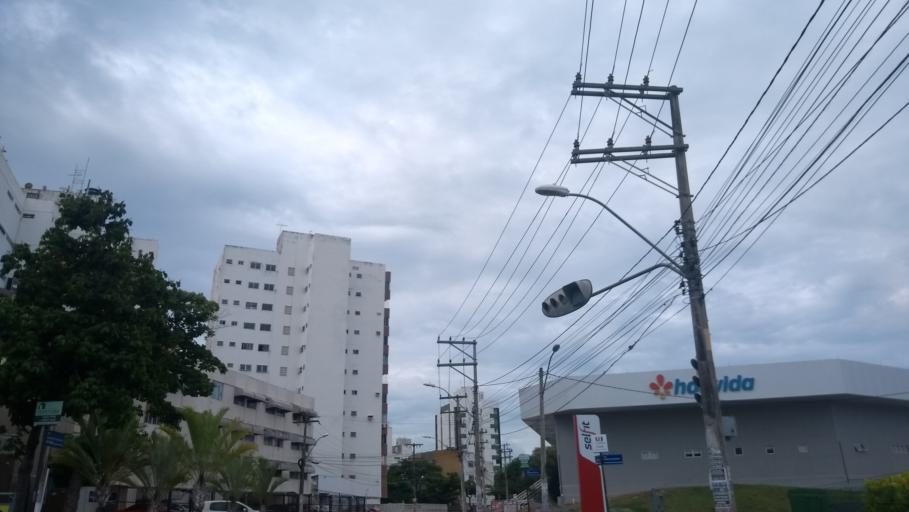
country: BR
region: Bahia
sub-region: Salvador
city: Salvador
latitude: -12.9925
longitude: -38.4483
